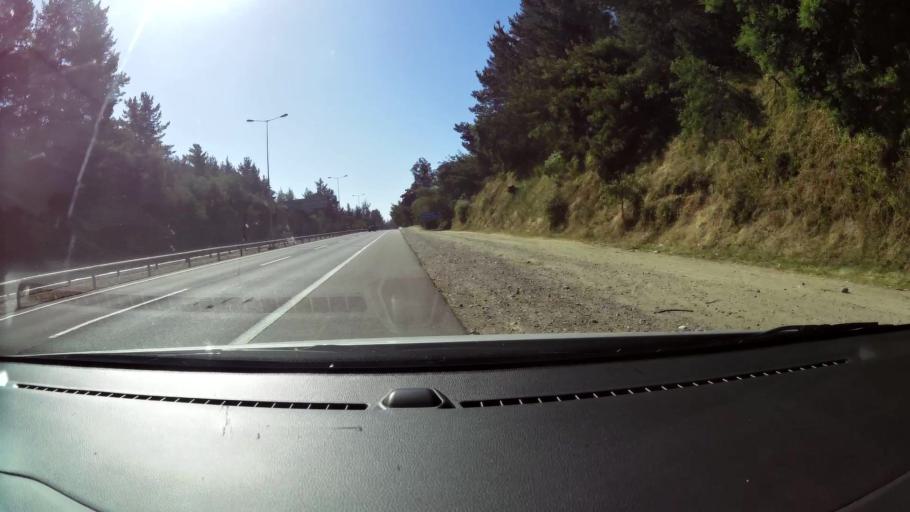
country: CL
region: Valparaiso
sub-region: Provincia de Valparaiso
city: Vina del Mar
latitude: -33.1602
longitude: -71.5439
